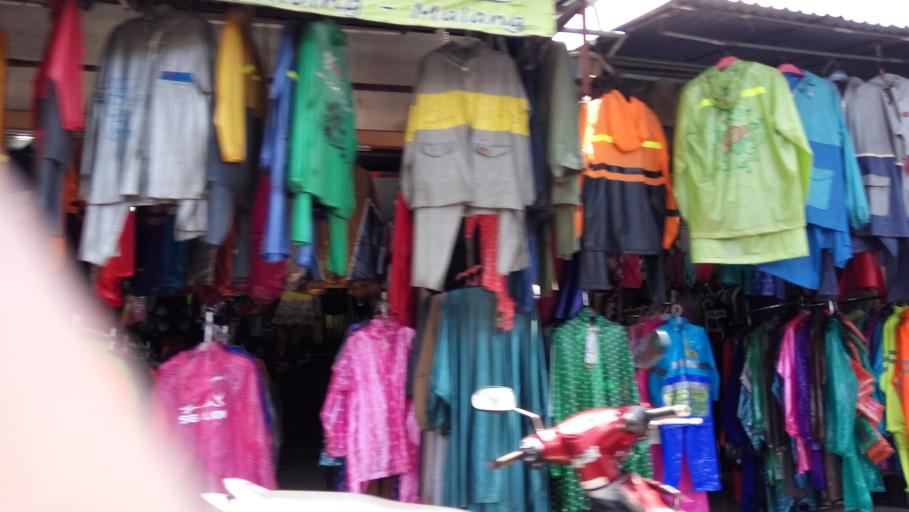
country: ID
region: East Java
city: Malang
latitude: -7.9403
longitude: 112.6392
